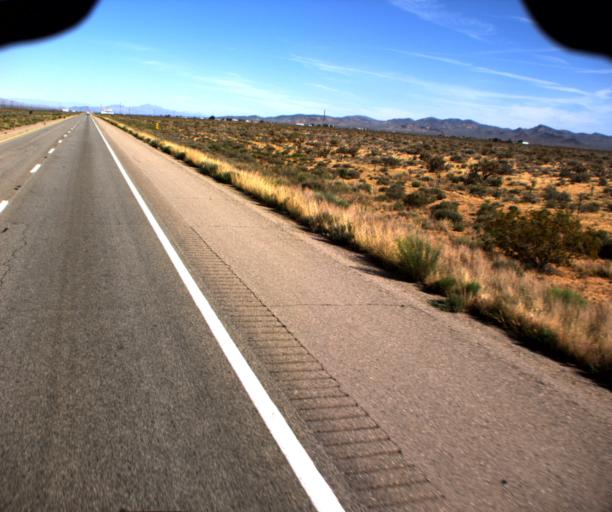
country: US
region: Arizona
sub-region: Mohave County
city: Dolan Springs
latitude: 35.5224
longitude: -114.3472
